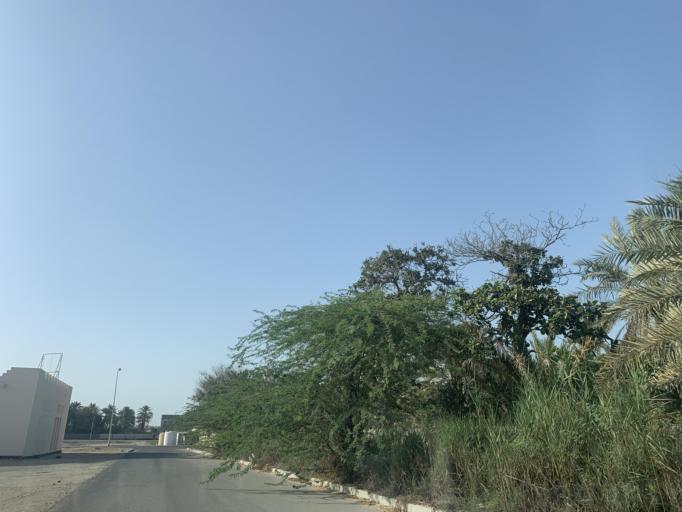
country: BH
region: Central Governorate
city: Madinat Hamad
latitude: 26.1899
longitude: 50.4583
